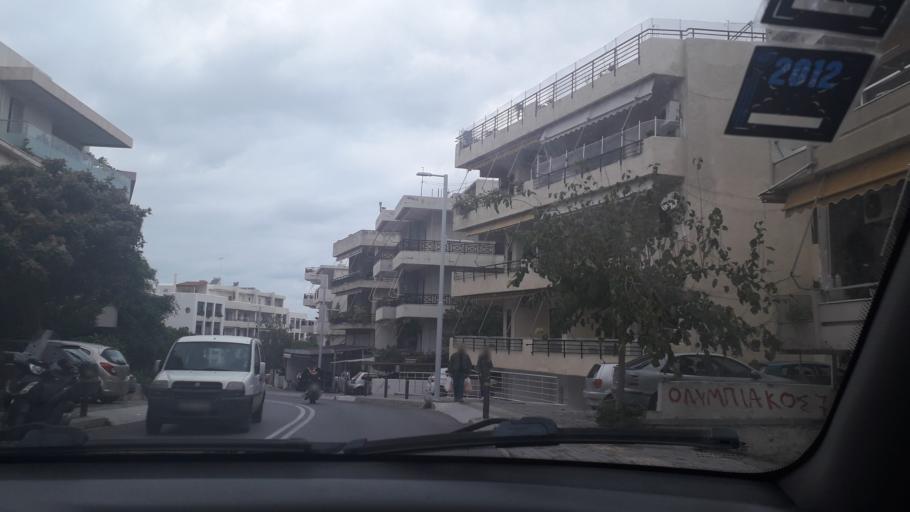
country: GR
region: Crete
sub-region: Nomos Rethymnis
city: Rethymno
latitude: 35.3609
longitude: 24.4739
